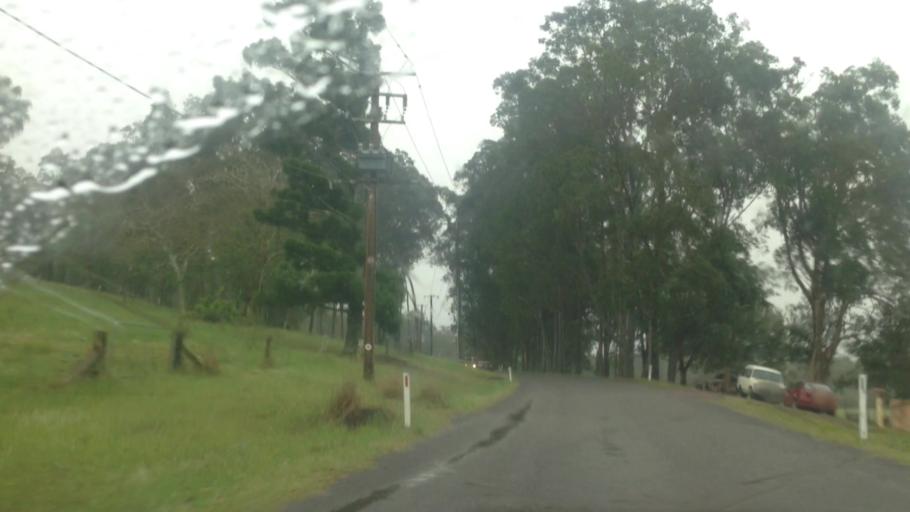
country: AU
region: New South Wales
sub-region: Wyong Shire
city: Little Jilliby
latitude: -33.2102
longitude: 151.3698
